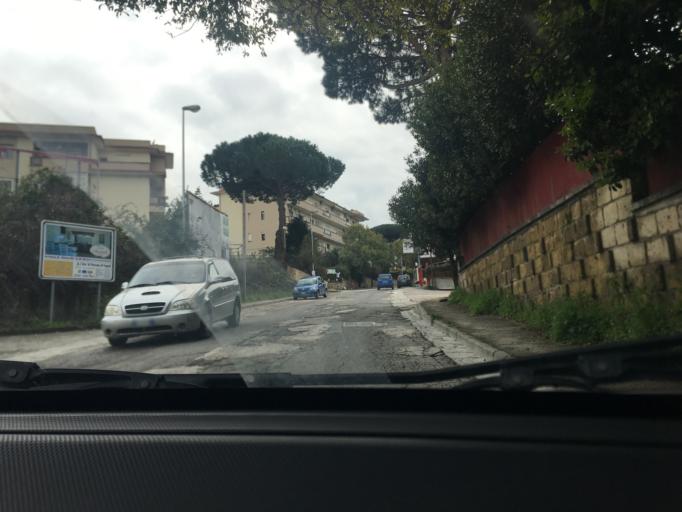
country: IT
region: Campania
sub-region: Provincia di Napoli
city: Marano di Napoli
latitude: 40.8933
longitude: 14.1811
